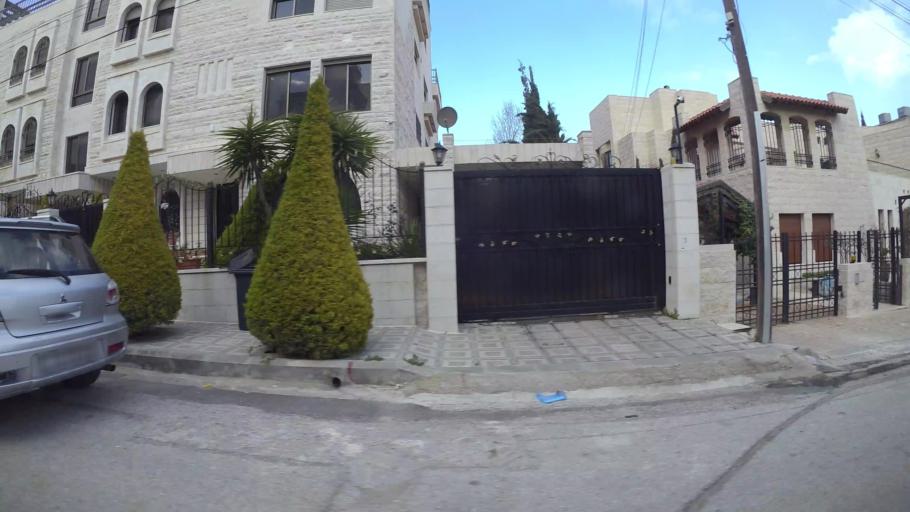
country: JO
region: Amman
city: Al Jubayhah
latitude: 31.9801
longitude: 35.8599
